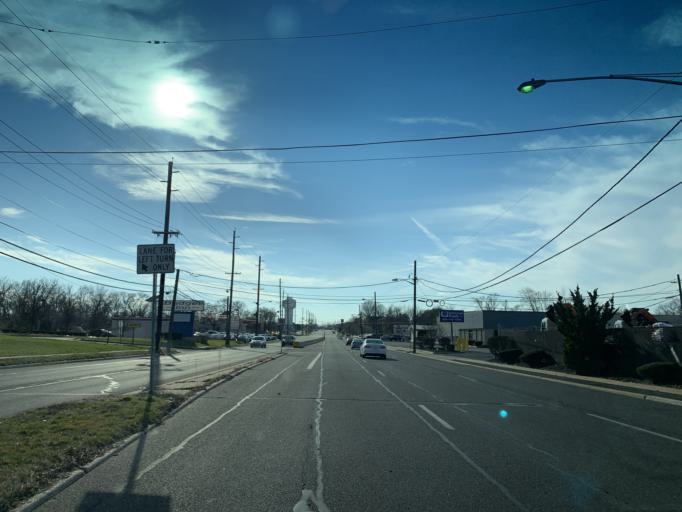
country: US
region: New Jersey
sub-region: Camden County
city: Gloucester City
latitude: 39.8827
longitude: -75.1105
